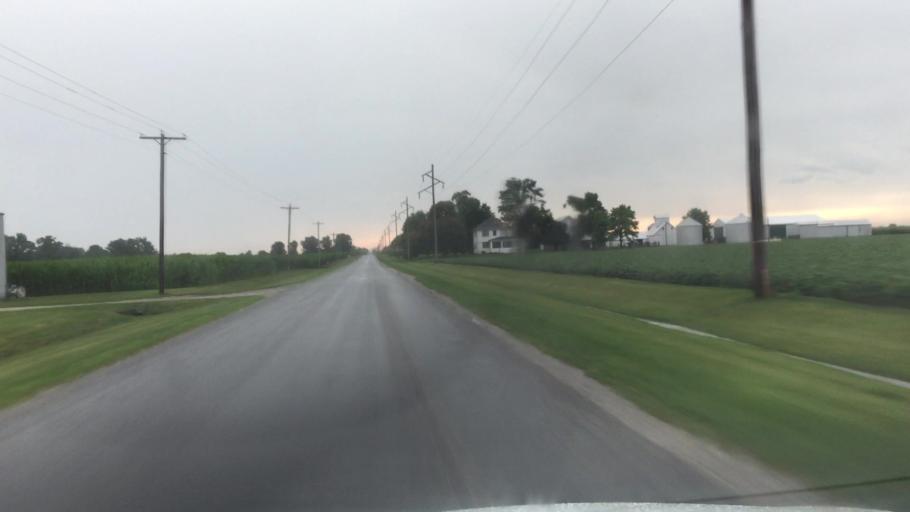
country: US
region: Illinois
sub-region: Hancock County
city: Hamilton
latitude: 40.4259
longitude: -91.2716
